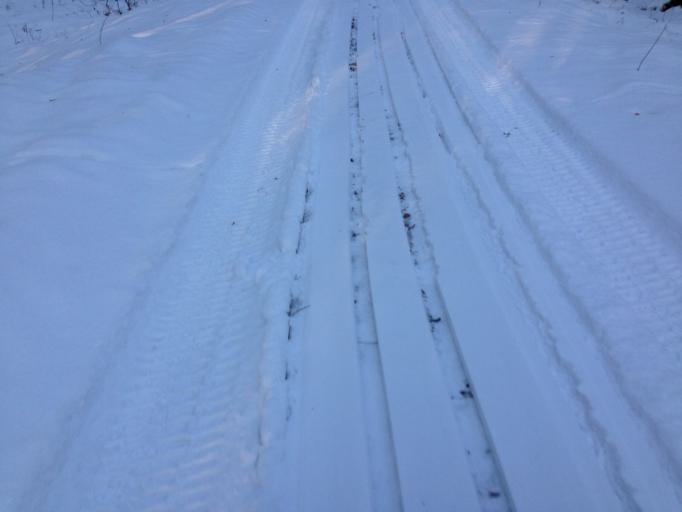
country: PL
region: Kujawsko-Pomorskie
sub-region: Powiat brodnicki
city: Gorzno
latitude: 53.1914
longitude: 19.6795
